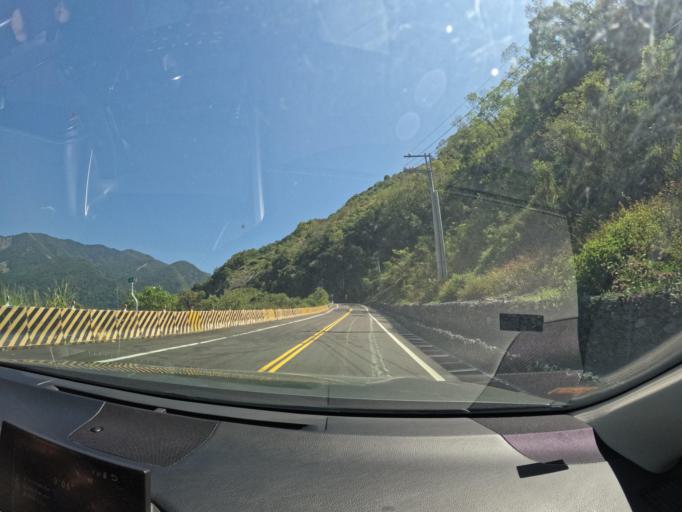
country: TW
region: Taiwan
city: Yujing
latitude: 23.2808
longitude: 120.8378
